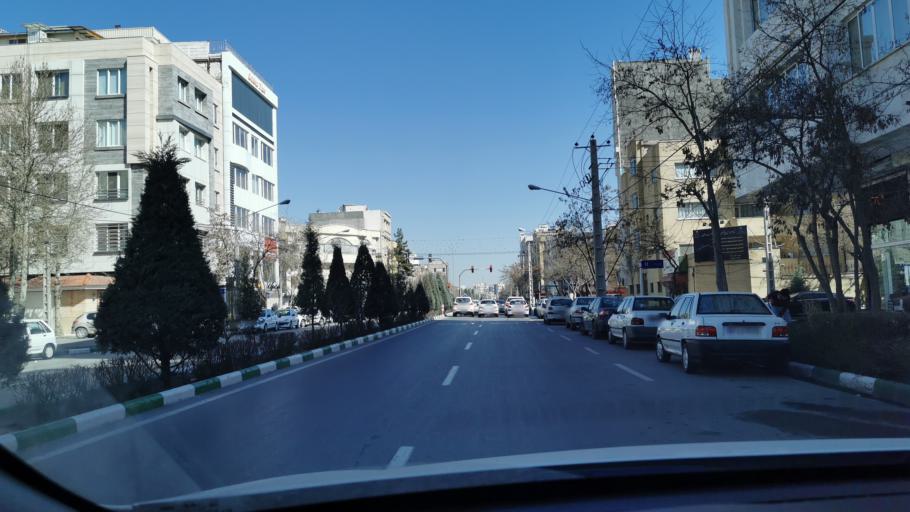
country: IR
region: Razavi Khorasan
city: Mashhad
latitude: 36.3235
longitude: 59.5262
